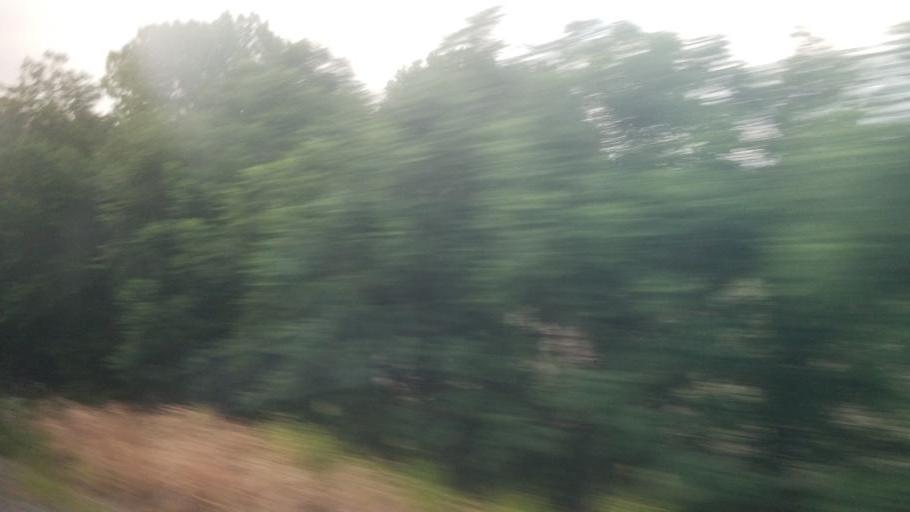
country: US
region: Kansas
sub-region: Marion County
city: Peabody
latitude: 38.1654
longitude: -97.0944
